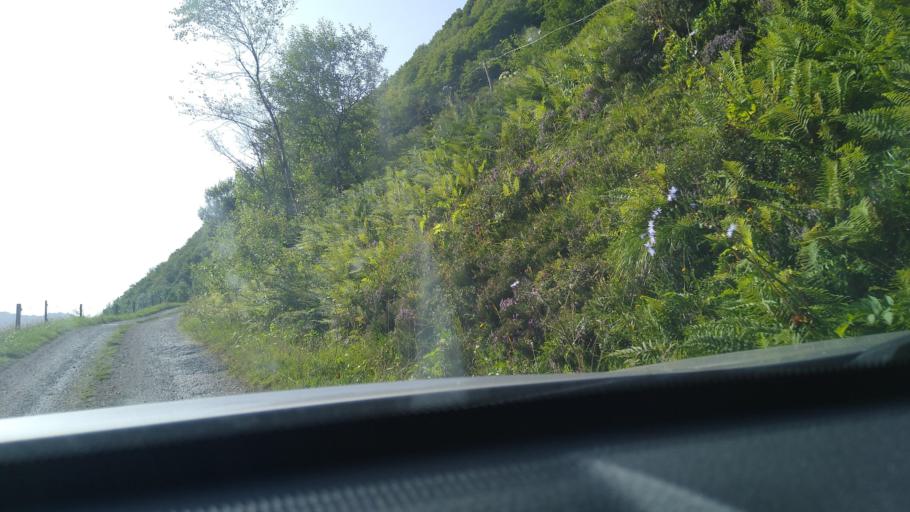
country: FR
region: Midi-Pyrenees
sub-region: Departement de l'Ariege
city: Saint-Girons
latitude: 42.7898
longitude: 1.1442
